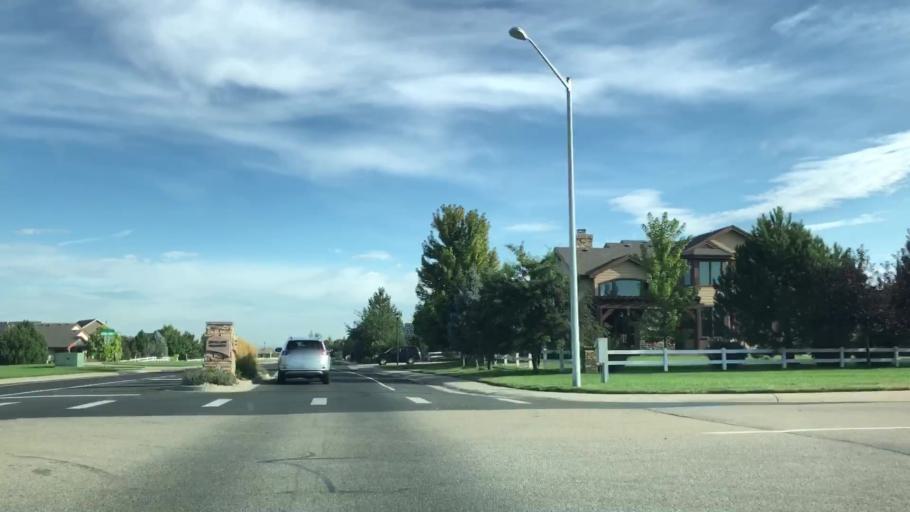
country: US
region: Colorado
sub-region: Weld County
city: Windsor
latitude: 40.4647
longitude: -104.9769
